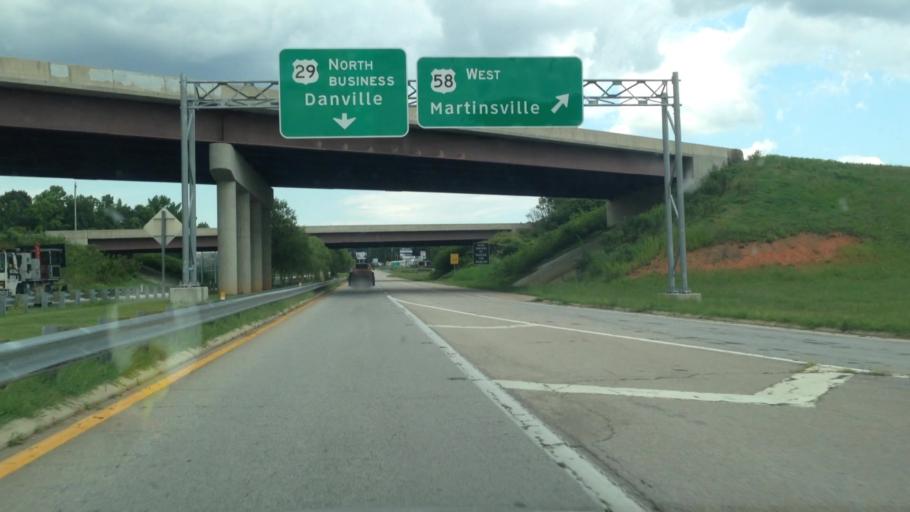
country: US
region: Virginia
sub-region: City of Danville
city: Danville
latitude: 36.5413
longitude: -79.4653
